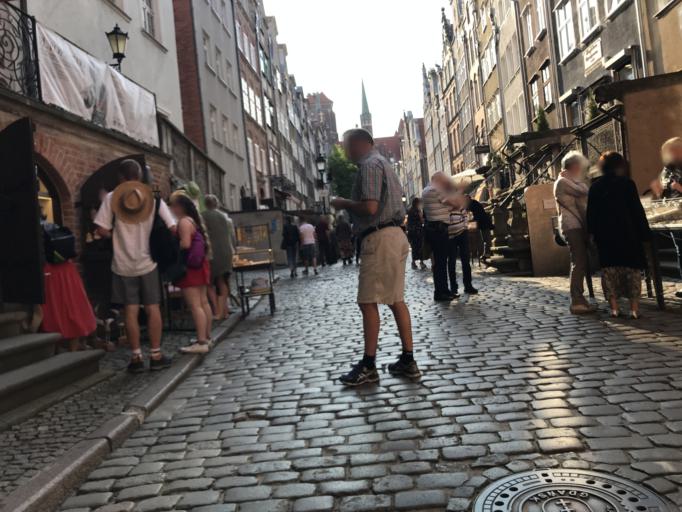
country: PL
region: Pomeranian Voivodeship
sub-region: Gdansk
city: Gdansk
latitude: 54.3495
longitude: 18.6566
